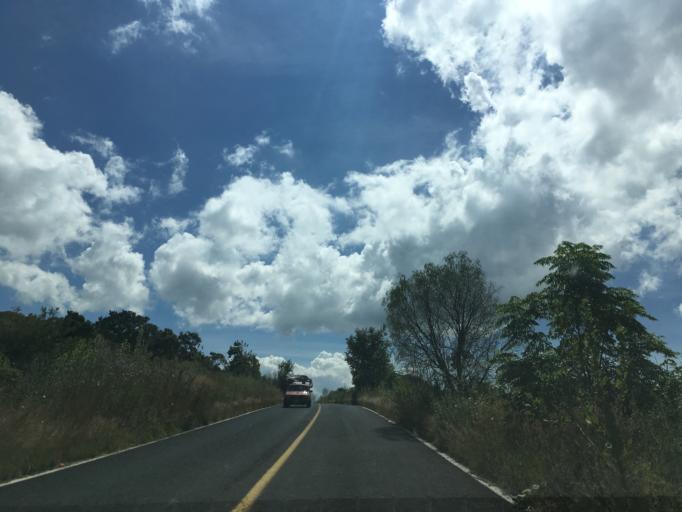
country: MX
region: Michoacan
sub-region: Morelia
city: Cuto de la Esperanza
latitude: 19.7475
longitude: -101.3692
